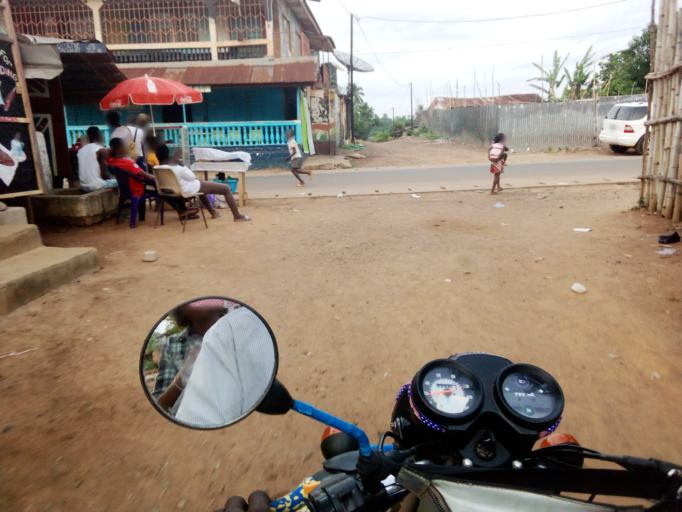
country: SL
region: Western Area
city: Waterloo
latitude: 8.3335
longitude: -13.0699
